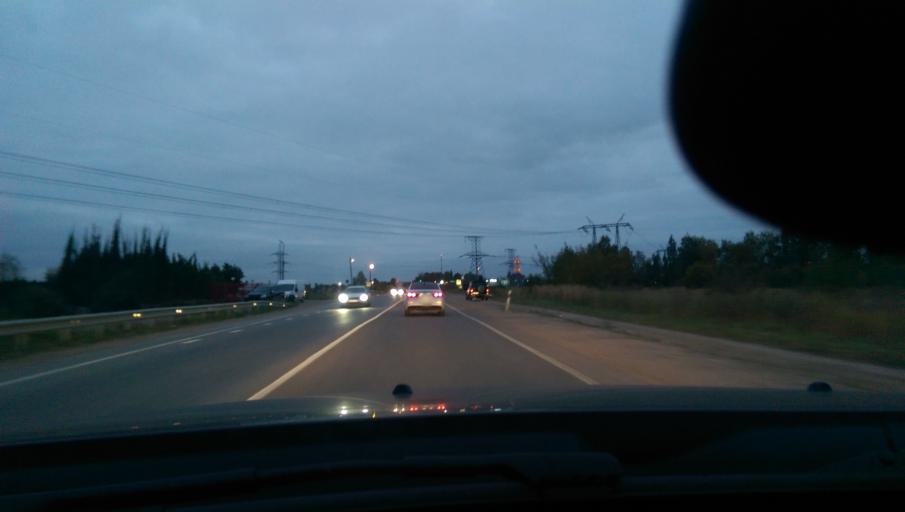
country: RU
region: Moskovskaya
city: Povedniki
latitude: 55.9575
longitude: 37.6539
